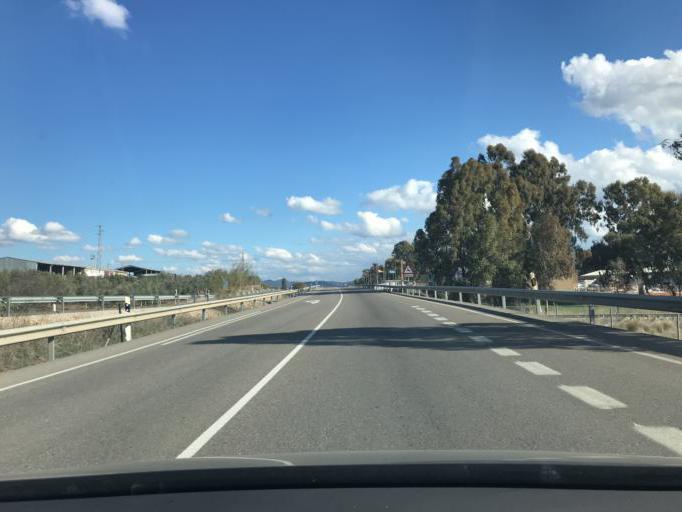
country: ES
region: Andalusia
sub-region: Province of Cordoba
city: Penarroya-Pueblonuevo
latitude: 38.2980
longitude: -5.2493
